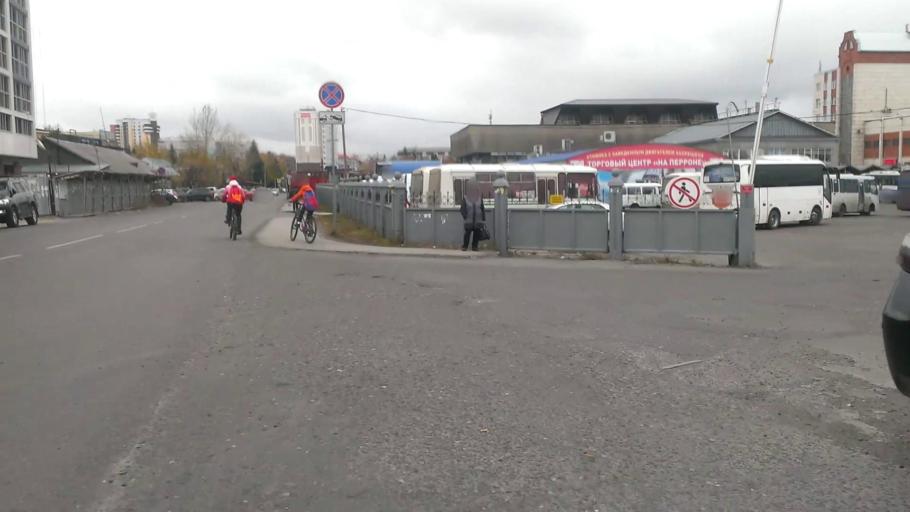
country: RU
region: Altai Krai
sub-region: Gorod Barnaulskiy
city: Barnaul
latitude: 53.3529
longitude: 83.7600
